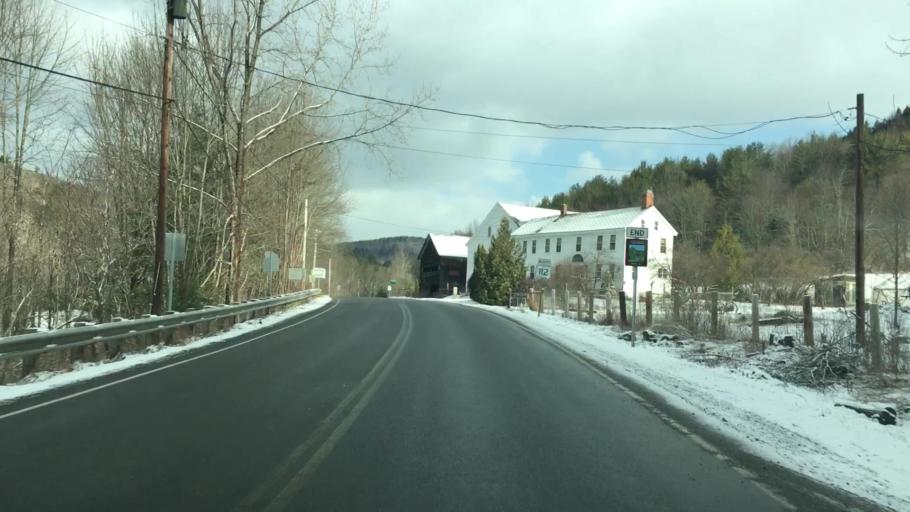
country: US
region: Massachusetts
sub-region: Franklin County
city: Colrain
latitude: 42.7337
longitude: -72.7207
